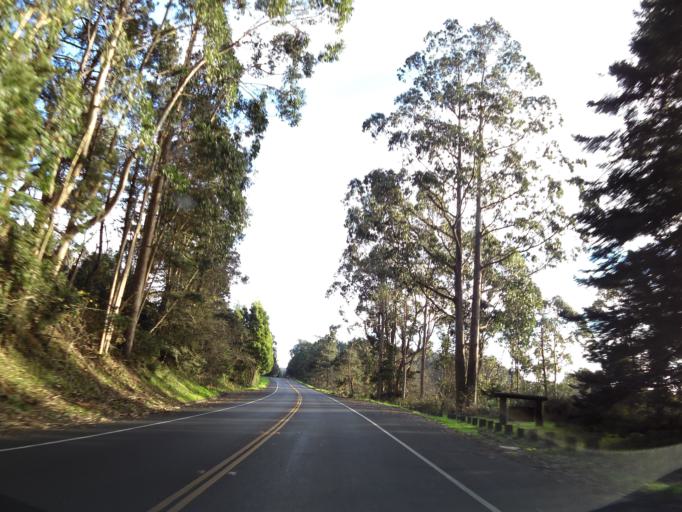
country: US
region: California
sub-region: Mendocino County
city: Fort Bragg
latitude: 39.3276
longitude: -123.8042
